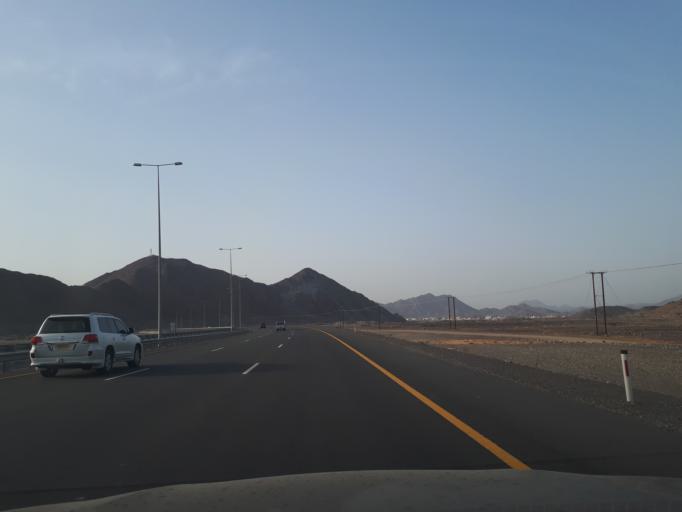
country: OM
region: Muhafazat ad Dakhiliyah
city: Sufalat Sama'il
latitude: 23.3038
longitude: 58.1110
